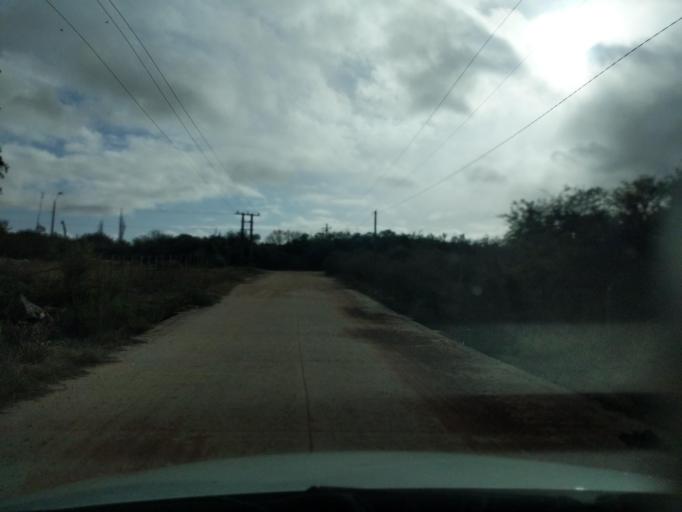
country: UY
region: Florida
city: Florida
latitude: -34.0597
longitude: -56.2161
